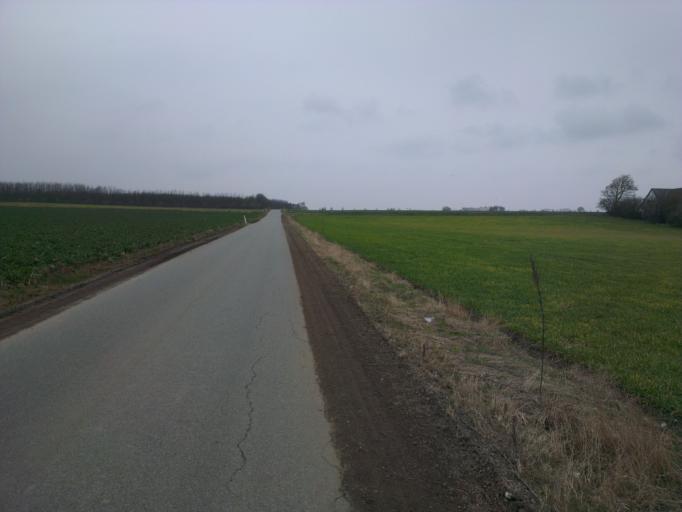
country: DK
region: Capital Region
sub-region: Frederikssund Kommune
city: Frederikssund
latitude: 55.8199
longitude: 12.1125
